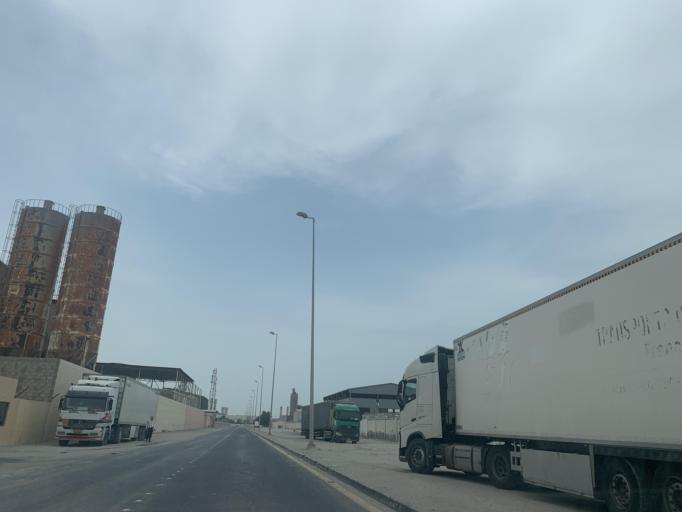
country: BH
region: Muharraq
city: Al Hadd
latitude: 26.2055
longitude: 50.6628
